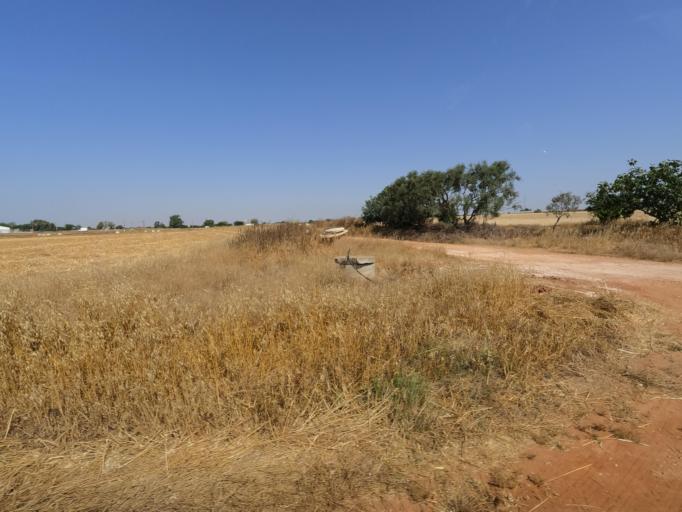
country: CY
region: Ammochostos
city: Liopetri
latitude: 34.9963
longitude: 33.9365
